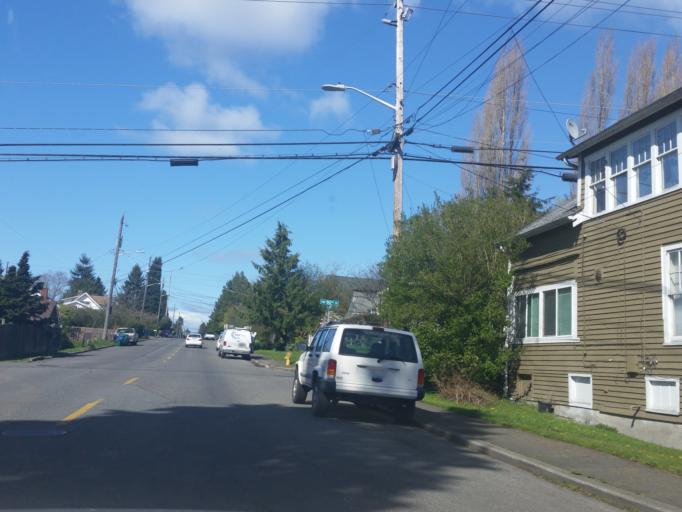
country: US
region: Washington
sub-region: King County
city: Shoreline
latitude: 47.6957
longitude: -122.3607
